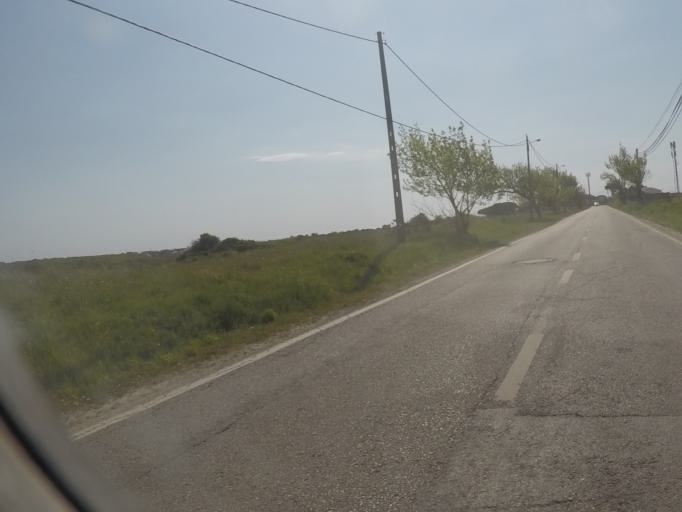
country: PT
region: Setubal
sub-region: Sesimbra
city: Sesimbra
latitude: 38.4463
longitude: -9.1555
